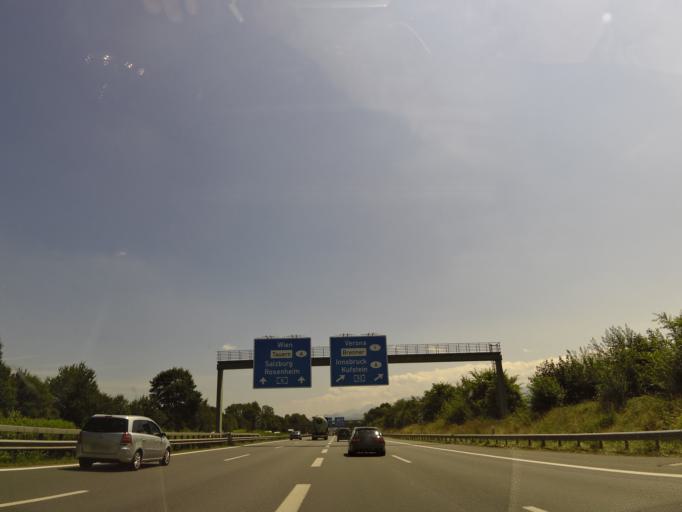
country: DE
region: Bavaria
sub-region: Upper Bavaria
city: Raubling
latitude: 47.8117
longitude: 12.0842
